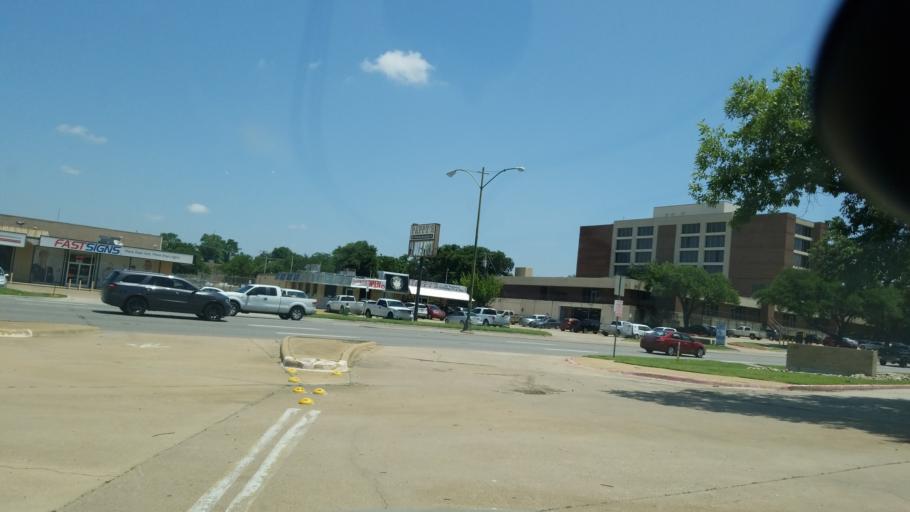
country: US
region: Texas
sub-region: Dallas County
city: Dallas
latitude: 32.8219
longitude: -96.8617
